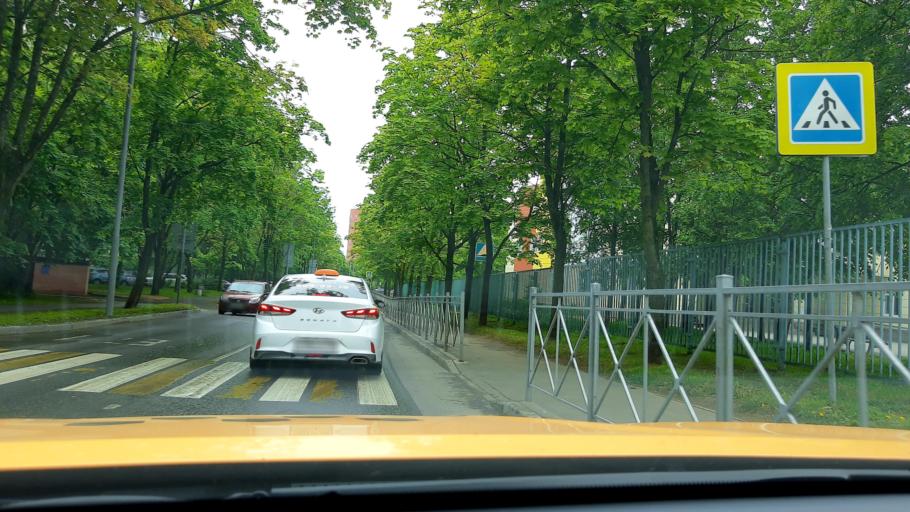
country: RU
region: Moskovskaya
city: Troitsk
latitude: 55.4868
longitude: 37.3013
